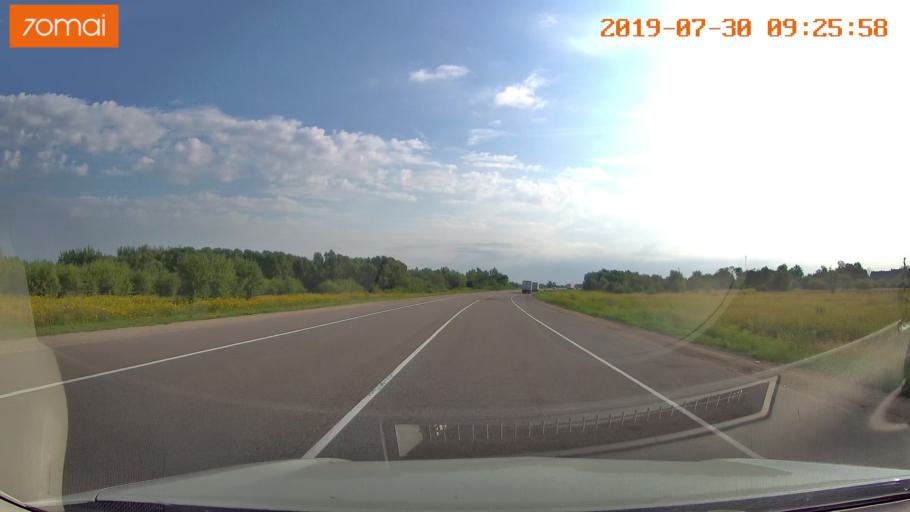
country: LT
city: Kybartai
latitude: 54.6441
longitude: 22.7223
